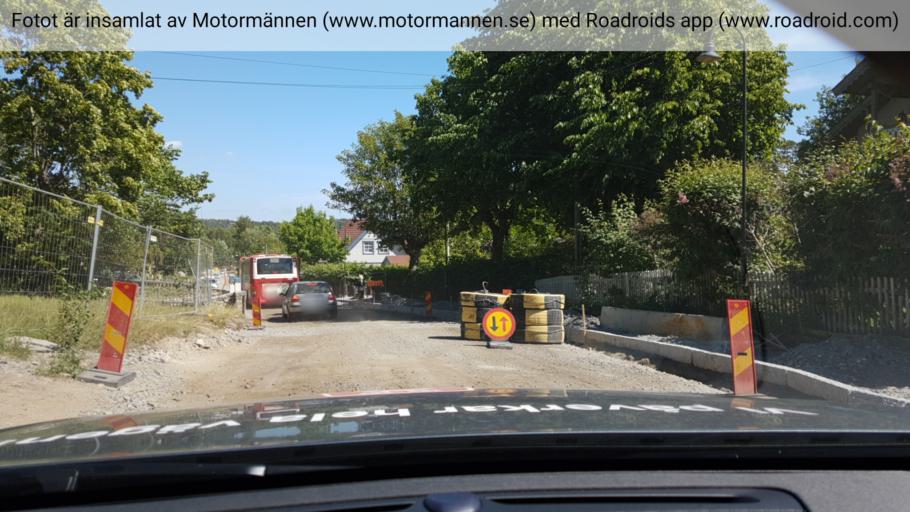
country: SE
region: Stockholm
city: Dalaro
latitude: 59.1354
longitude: 18.4110
